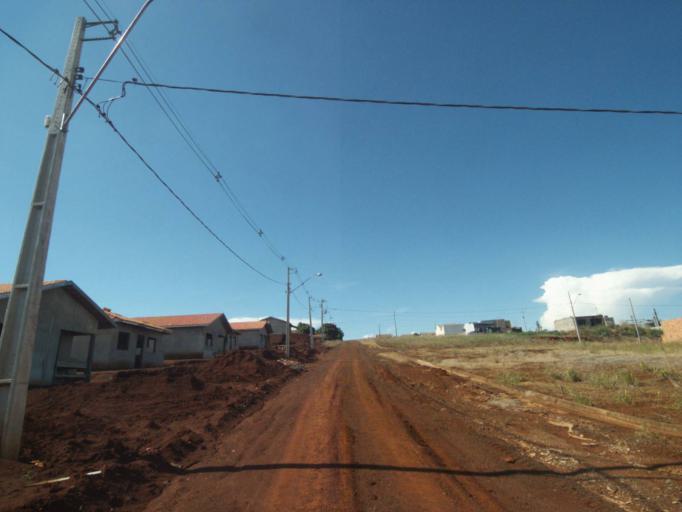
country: BR
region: Parana
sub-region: Sertanopolis
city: Sertanopolis
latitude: -23.0475
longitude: -50.8176
